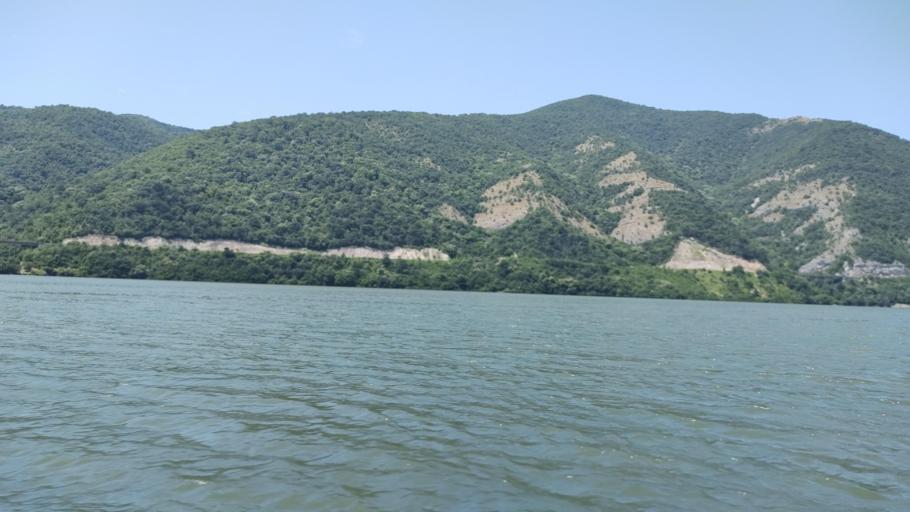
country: RO
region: Caras-Severin
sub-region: Comuna Berzasca
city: Berzasca
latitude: 44.5757
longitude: 22.0292
